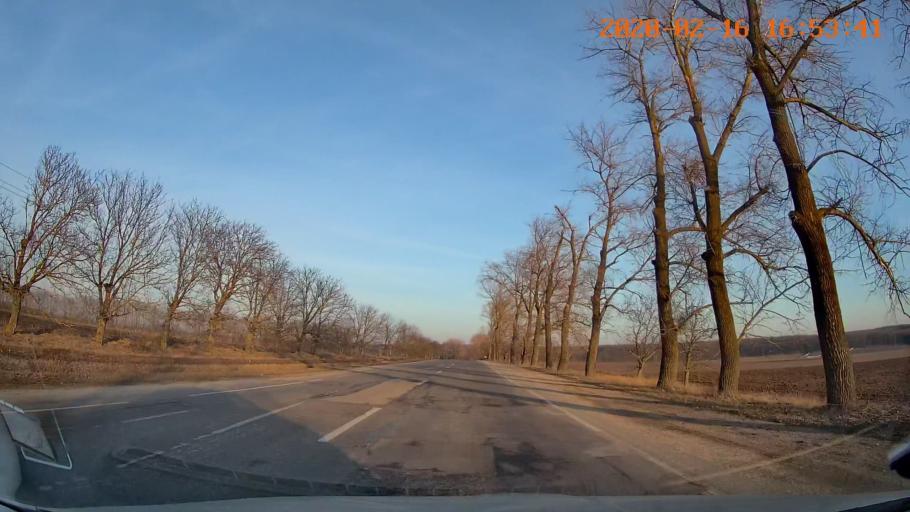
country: MD
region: Briceni
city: Briceni
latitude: 48.3163
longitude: 26.9906
